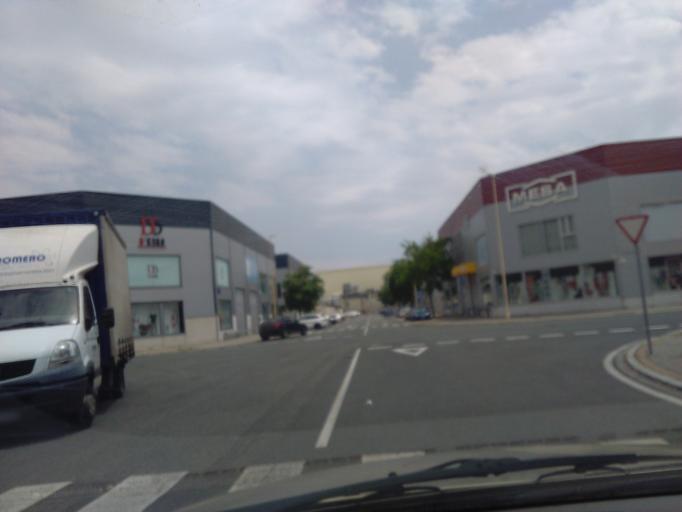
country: ES
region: Andalusia
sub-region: Provincia de Sevilla
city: Sevilla
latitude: 37.3837
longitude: -5.9318
